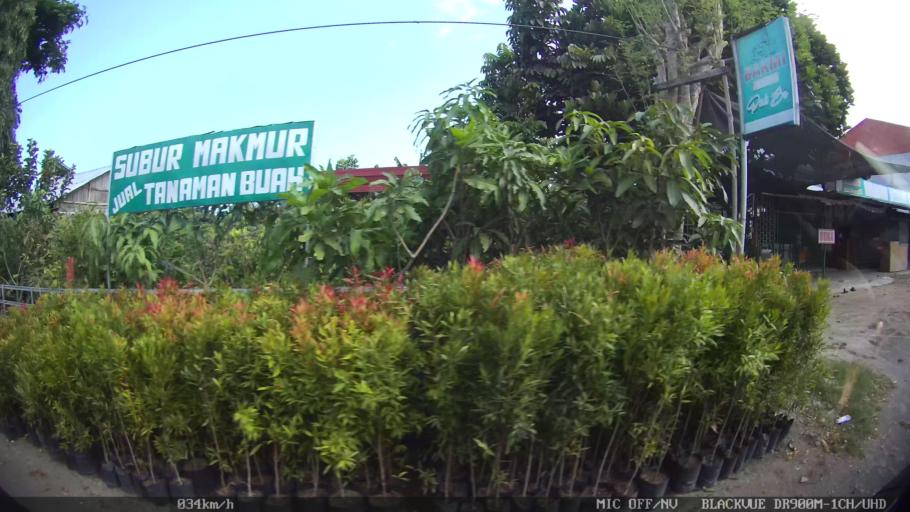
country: ID
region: Daerah Istimewa Yogyakarta
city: Sewon
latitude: -7.8677
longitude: 110.3499
